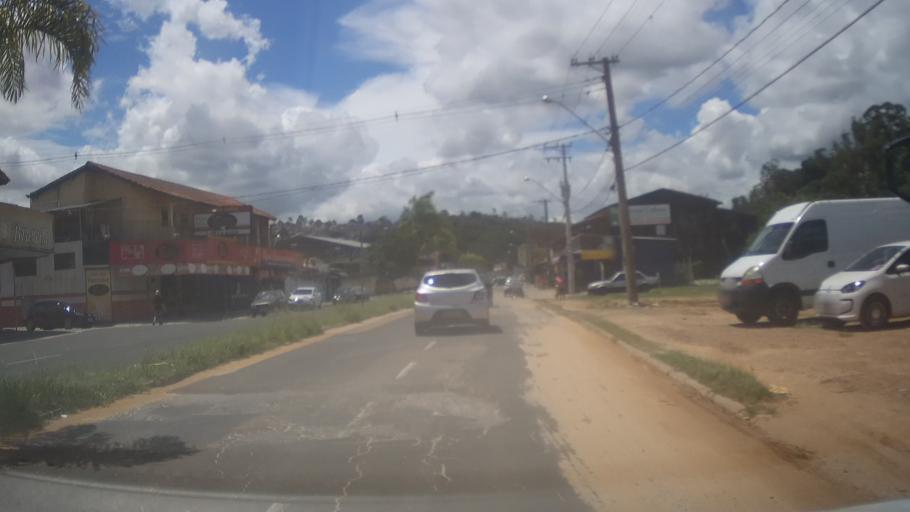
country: BR
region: Sao Paulo
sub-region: Campo Limpo Paulista
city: Campo Limpo Paulista
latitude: -23.2119
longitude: -46.7593
